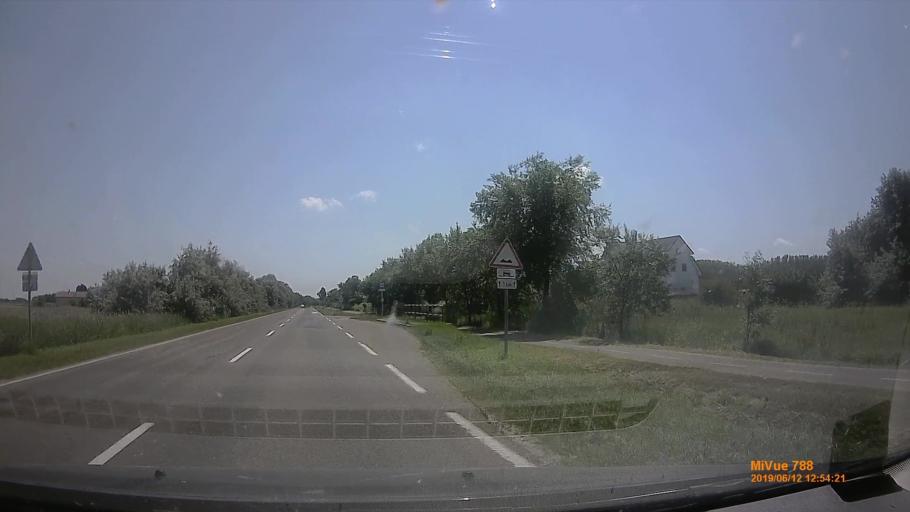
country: HU
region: Bacs-Kiskun
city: Kiskunfelegyhaza
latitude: 46.6722
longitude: 19.8562
